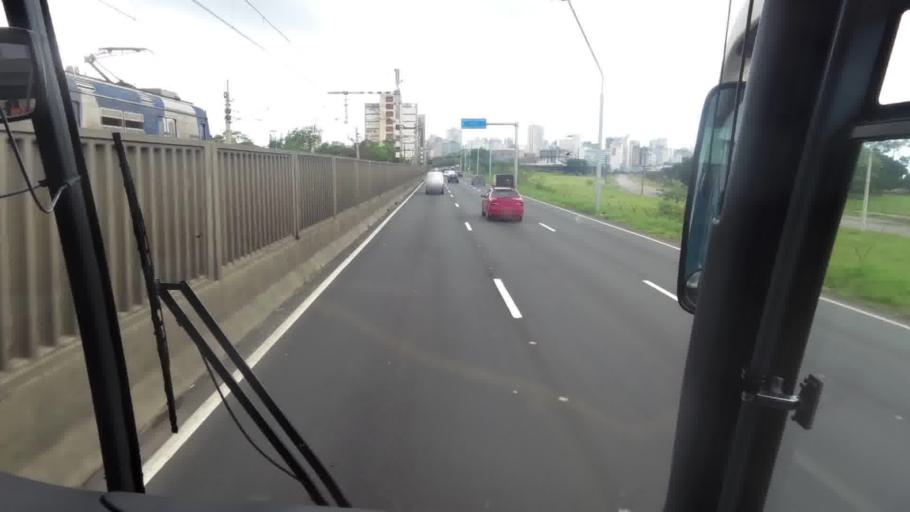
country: BR
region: Rio Grande do Sul
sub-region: Porto Alegre
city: Porto Alegre
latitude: -30.0180
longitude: -51.2155
